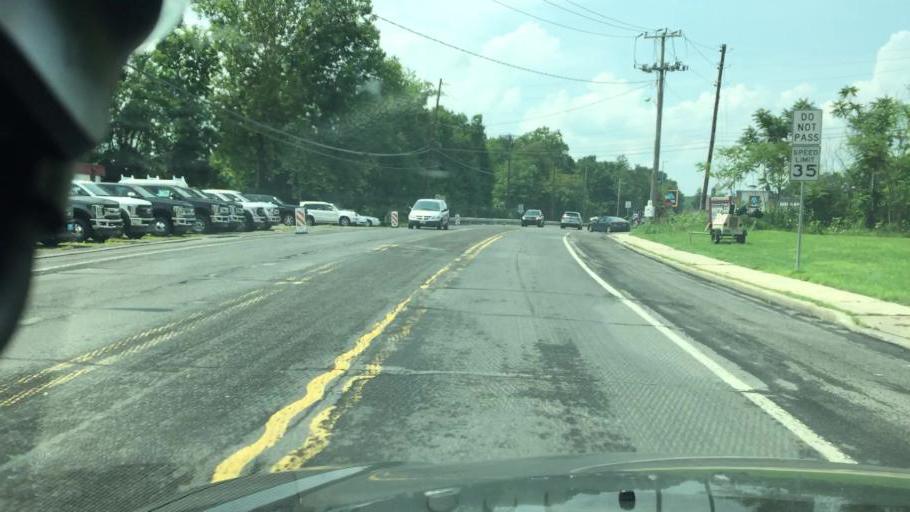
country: US
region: Pennsylvania
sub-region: Monroe County
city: Arlington Heights
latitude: 40.9871
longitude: -75.2064
